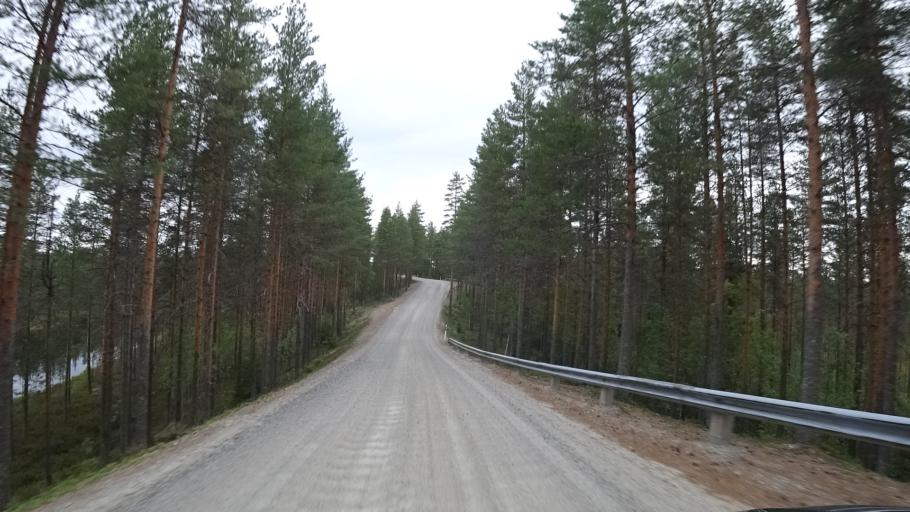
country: FI
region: North Karelia
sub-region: Pielisen Karjala
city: Lieksa
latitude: 63.2605
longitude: 30.3211
